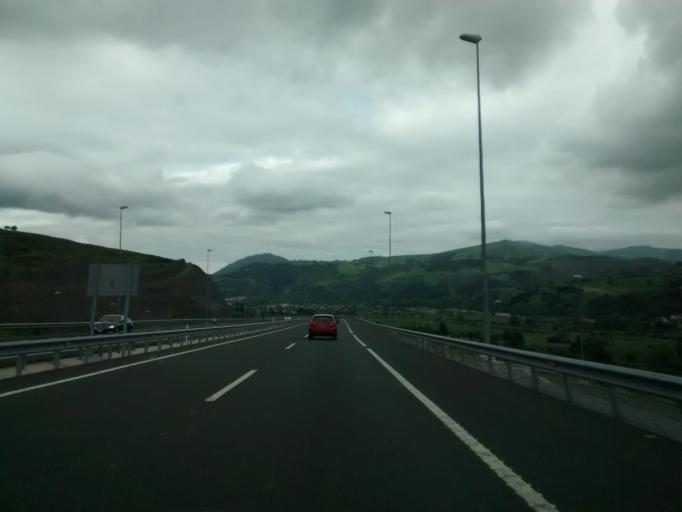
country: ES
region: Cantabria
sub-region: Provincia de Cantabria
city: Molledo
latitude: 43.1630
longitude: -4.0528
